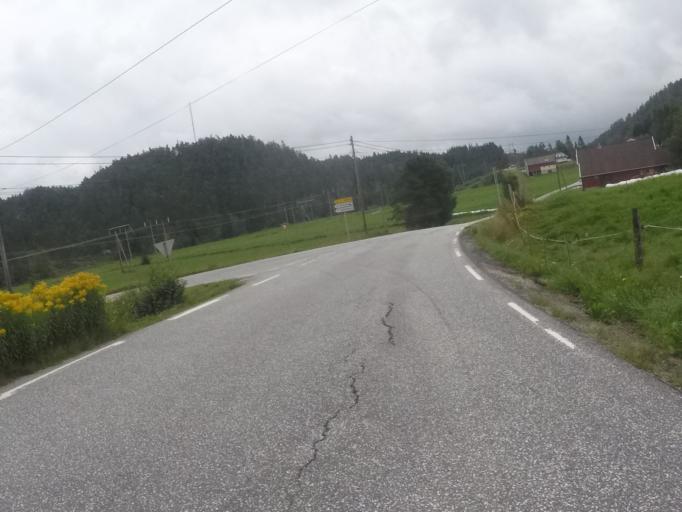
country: NO
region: Vest-Agder
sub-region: Marnardal
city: Helland
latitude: 58.2823
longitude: 7.6119
